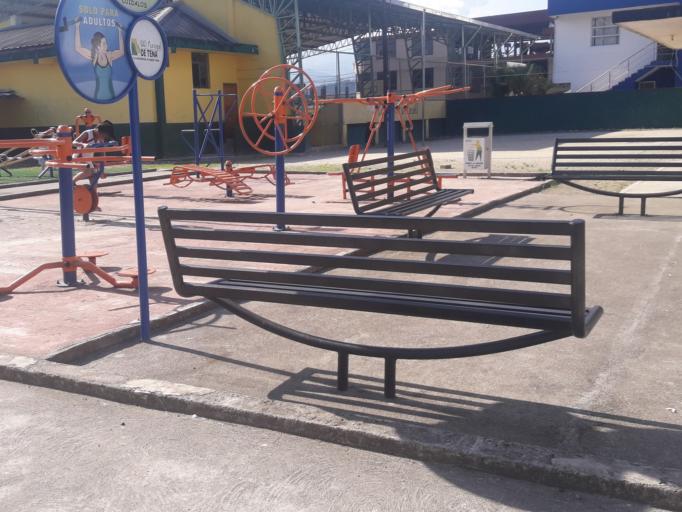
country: EC
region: Napo
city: Tena
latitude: -1.0046
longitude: -77.8133
